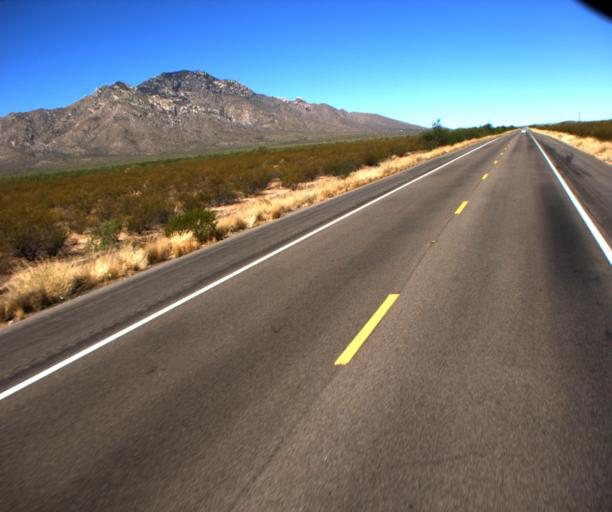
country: US
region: Arizona
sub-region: Pima County
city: Three Points
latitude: 32.0406
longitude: -111.4671
